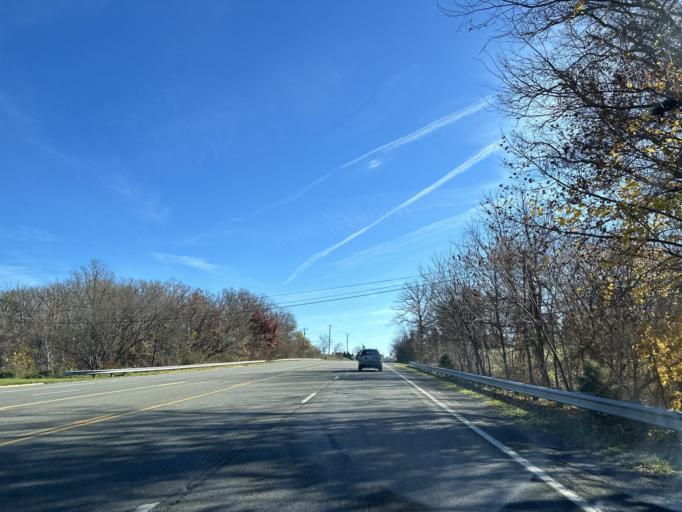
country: US
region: Virginia
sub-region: Augusta County
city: Fishersville
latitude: 38.1121
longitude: -79.0067
